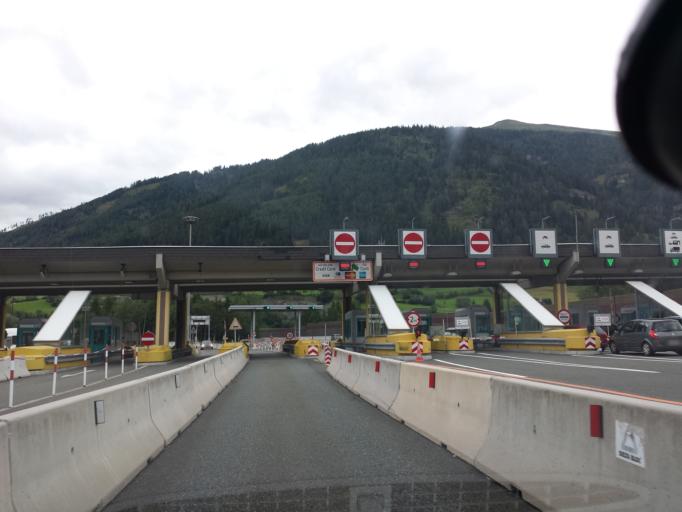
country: AT
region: Salzburg
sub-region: Politischer Bezirk Tamsweg
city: Sankt Michael im Lungau
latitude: 47.0938
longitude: 13.6095
